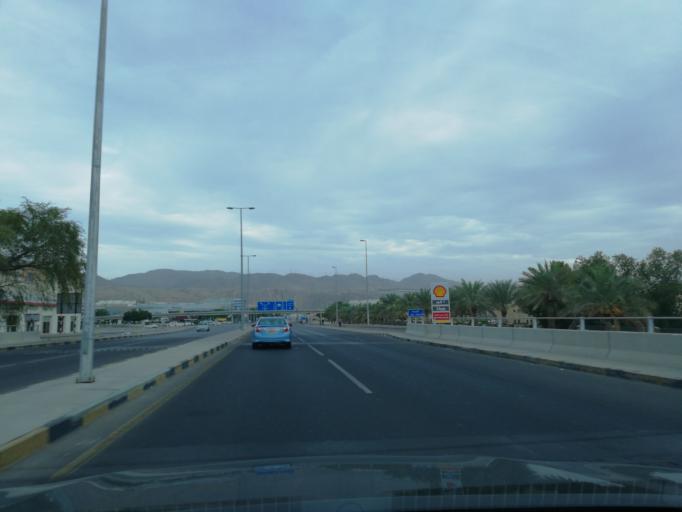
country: OM
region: Muhafazat Masqat
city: Muscat
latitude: 23.6150
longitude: 58.4940
